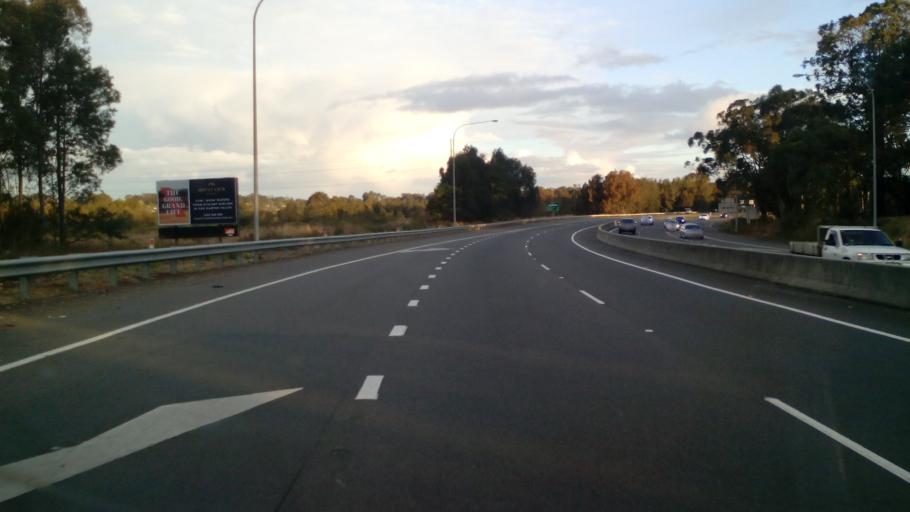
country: AU
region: New South Wales
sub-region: Newcastle
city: Beresfield
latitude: -32.7973
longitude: 151.6388
